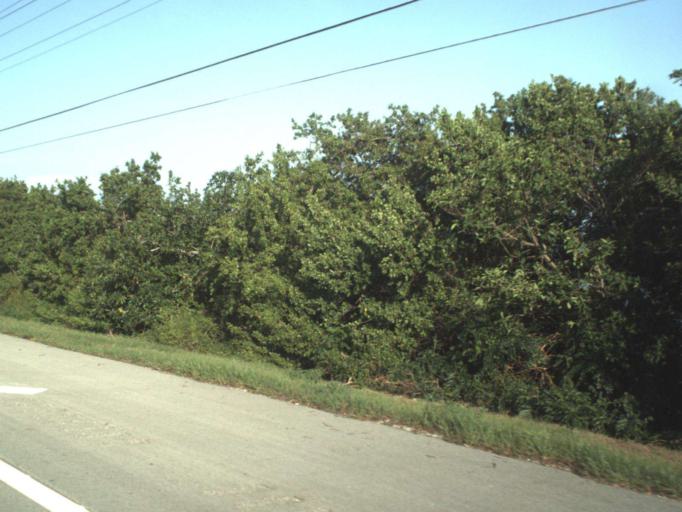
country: US
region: Florida
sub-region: Monroe County
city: Marathon
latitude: 24.7879
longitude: -80.8929
